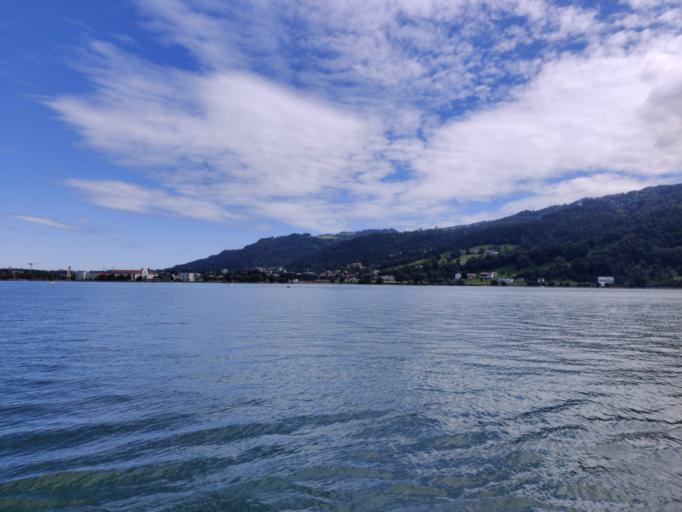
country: AT
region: Vorarlberg
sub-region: Politischer Bezirk Bregenz
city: Bregenz
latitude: 47.5173
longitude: 9.7389
